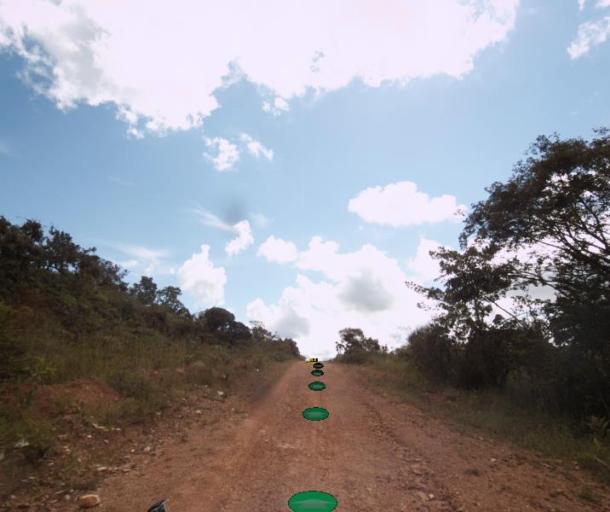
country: BR
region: Goias
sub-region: Pirenopolis
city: Pirenopolis
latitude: -15.7874
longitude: -48.9194
